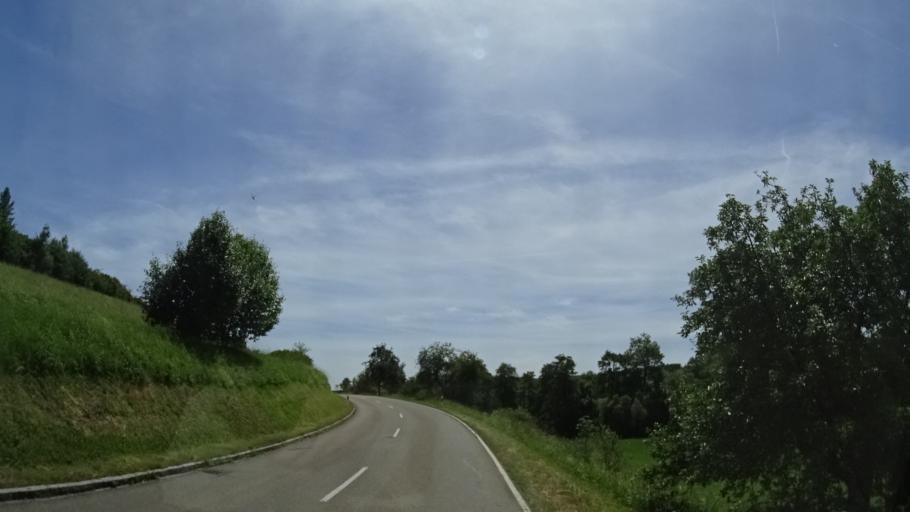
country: DE
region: Baden-Wuerttemberg
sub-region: Regierungsbezirk Stuttgart
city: Buhlerzell
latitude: 49.0092
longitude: 9.9159
